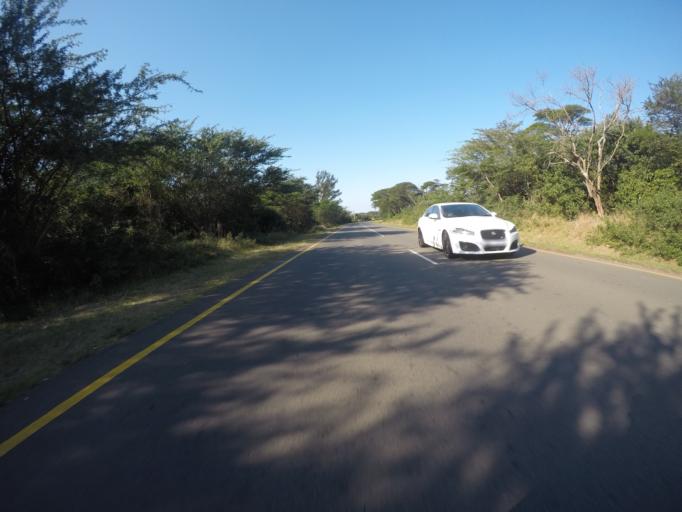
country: ZA
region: KwaZulu-Natal
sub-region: uThungulu District Municipality
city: Richards Bay
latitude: -28.7818
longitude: 32.0706
